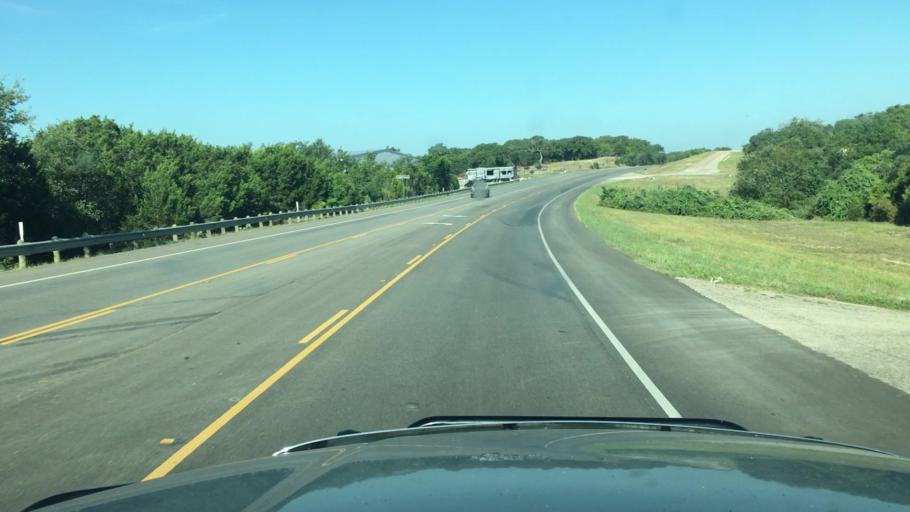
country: US
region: Texas
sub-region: Hays County
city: Dripping Springs
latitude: 30.1980
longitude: -98.1627
